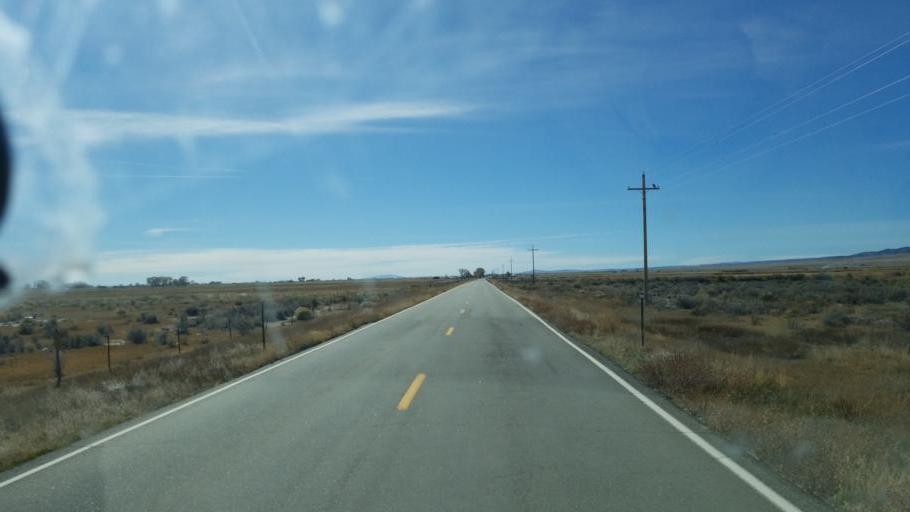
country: US
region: Colorado
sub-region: Rio Grande County
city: Monte Vista
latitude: 37.4730
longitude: -106.1488
